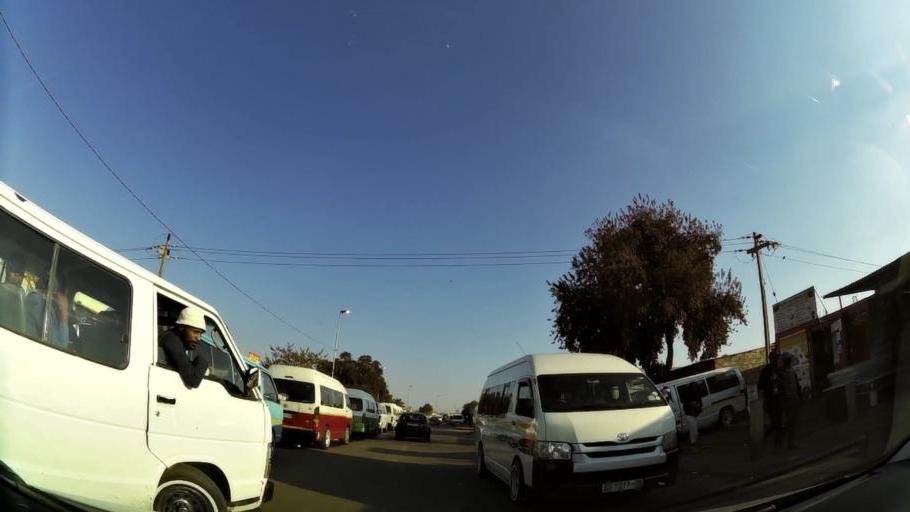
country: ZA
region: Gauteng
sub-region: Ekurhuleni Metropolitan Municipality
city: Tembisa
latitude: -25.9822
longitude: 28.2046
